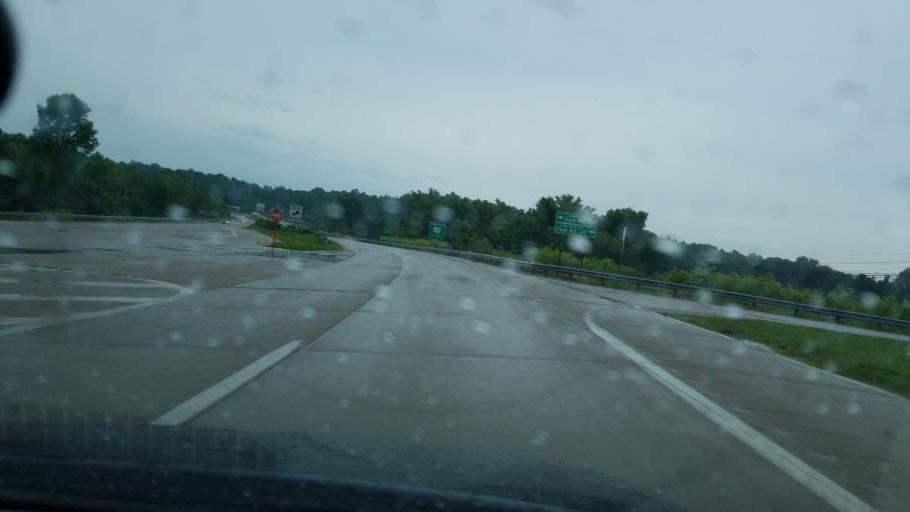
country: US
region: Ohio
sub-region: Athens County
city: Athens
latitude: 39.2843
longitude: -81.9271
